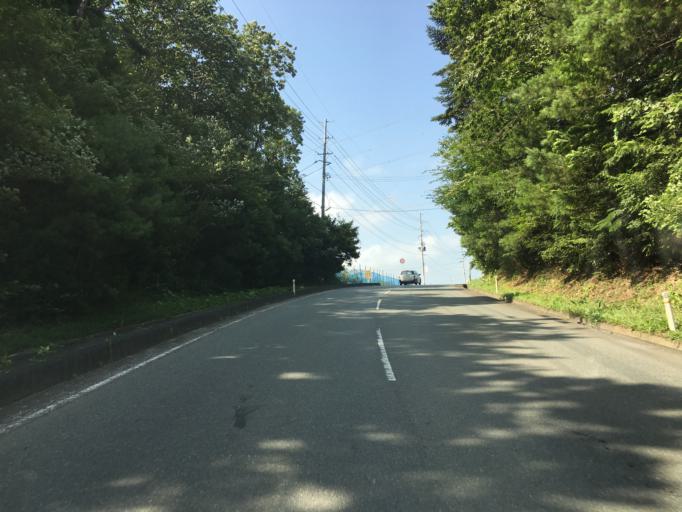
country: JP
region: Miyagi
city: Marumori
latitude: 37.8520
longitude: 140.8957
